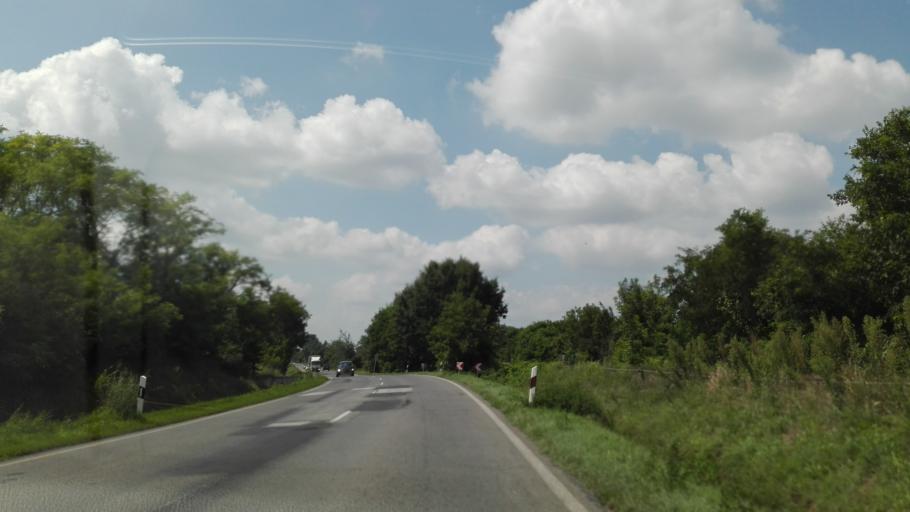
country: HU
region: Fejer
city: Eloszallas
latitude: 46.8271
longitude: 18.8580
